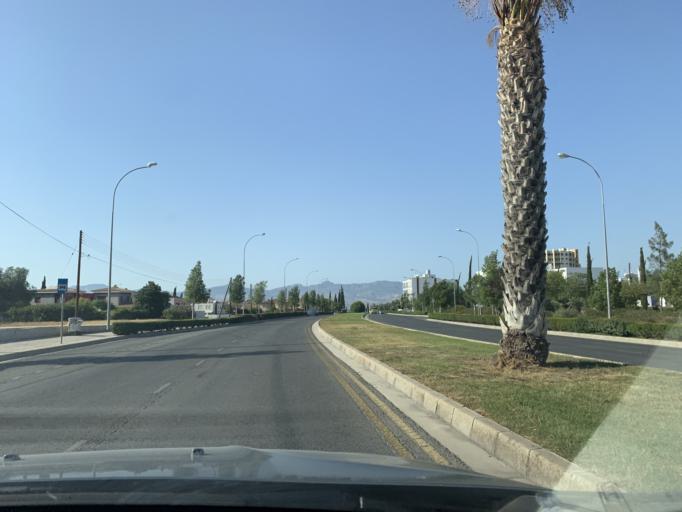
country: CY
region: Lefkosia
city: Nicosia
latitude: 35.1503
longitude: 33.3814
